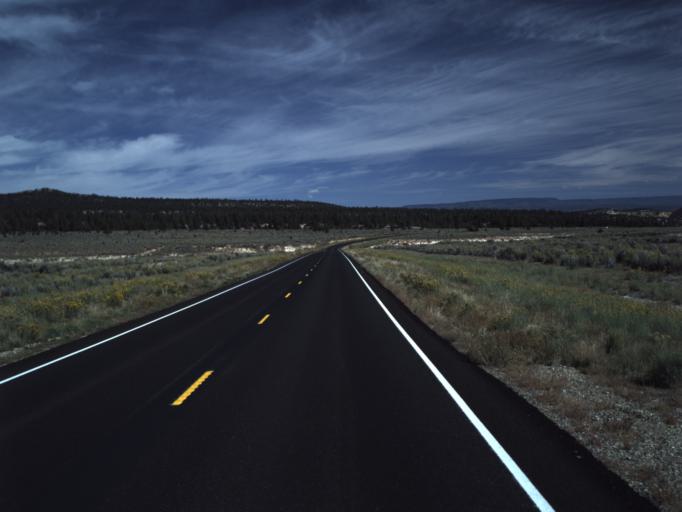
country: US
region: Utah
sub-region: Garfield County
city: Panguitch
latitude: 37.6681
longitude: -111.8304
